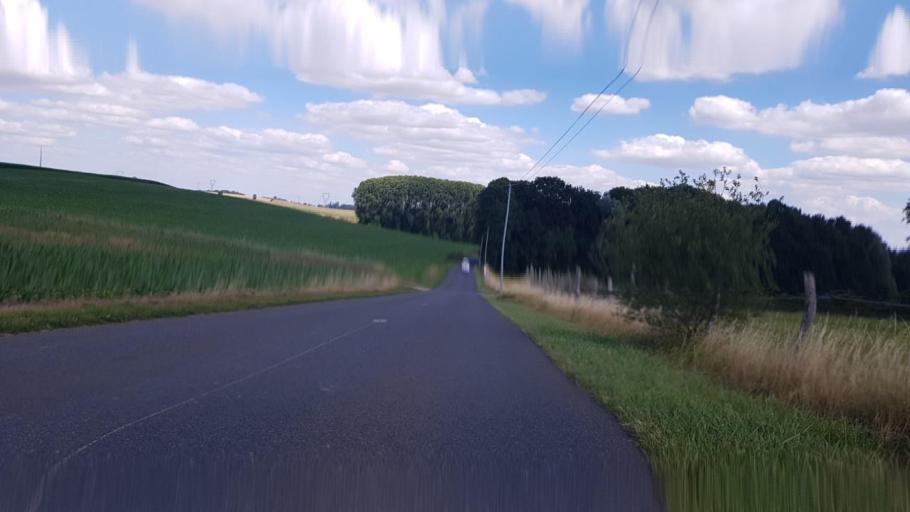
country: FR
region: Ile-de-France
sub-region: Departement de Seine-et-Marne
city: Moussy-le-Neuf
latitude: 49.0708
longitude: 2.6211
